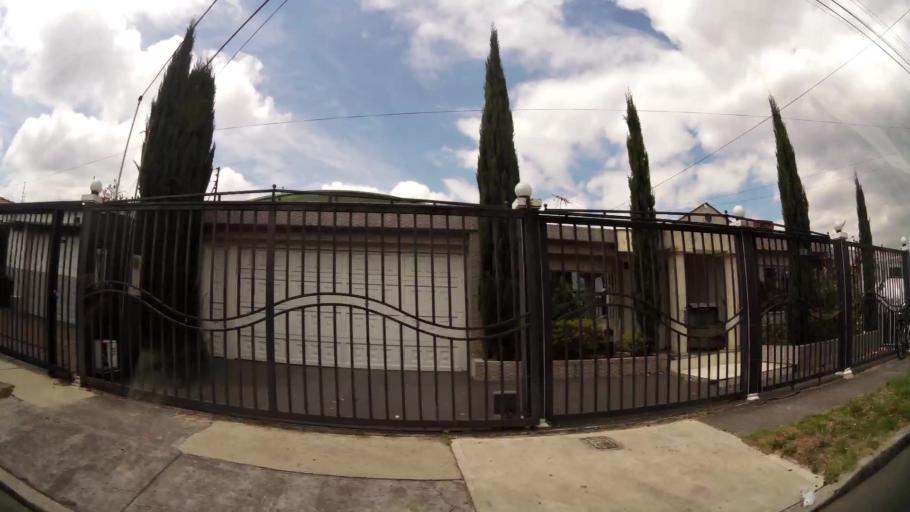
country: CO
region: Bogota D.C.
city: Barrio San Luis
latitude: 4.7024
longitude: -74.0613
